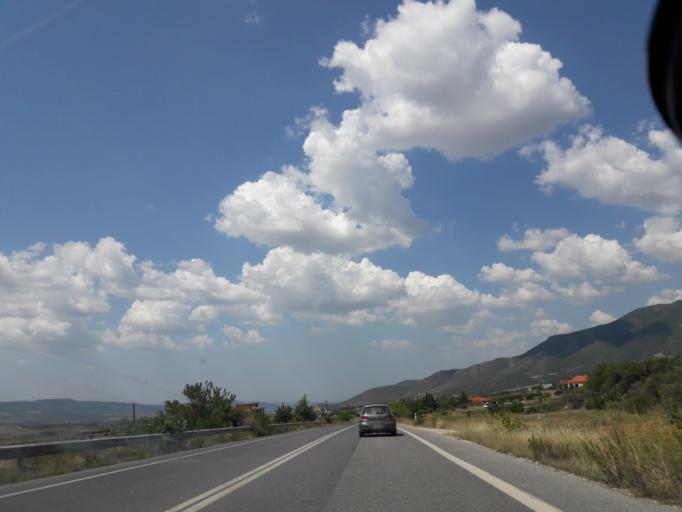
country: GR
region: Central Macedonia
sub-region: Nomos Chalkidikis
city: Galatista
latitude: 40.4639
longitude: 23.2671
